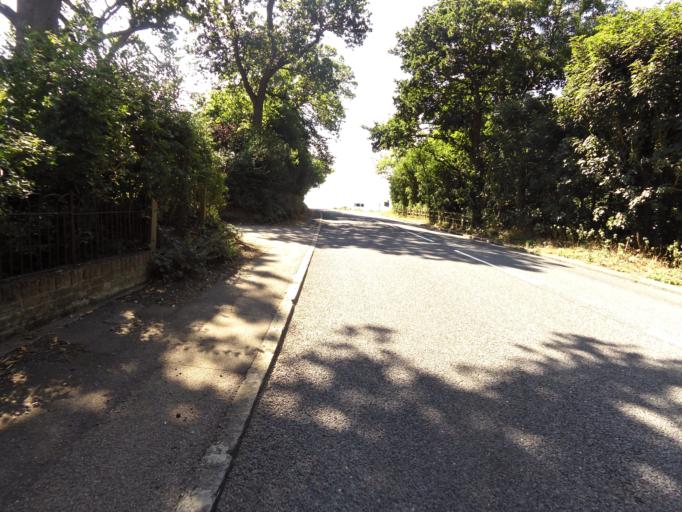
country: GB
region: England
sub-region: Suffolk
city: East Bergholt
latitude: 51.9604
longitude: 0.9657
